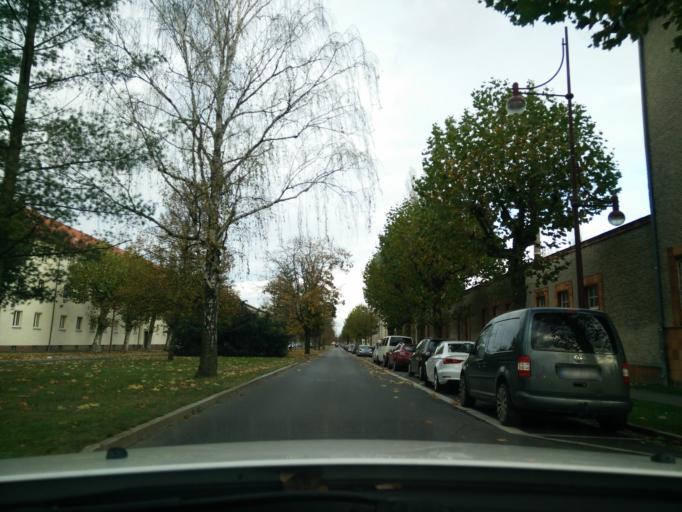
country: DE
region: Brandenburg
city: Velten
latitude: 52.6860
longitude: 13.1727
